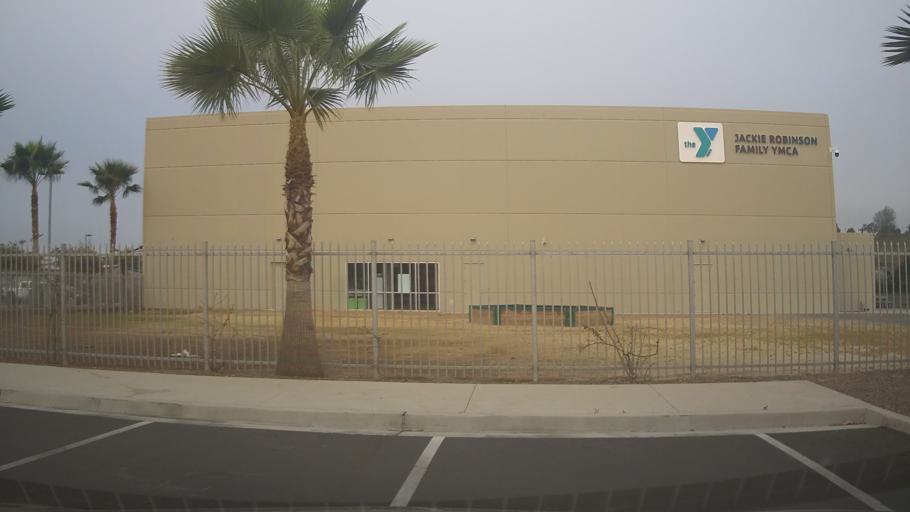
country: US
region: California
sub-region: San Diego County
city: National City
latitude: 32.7052
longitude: -117.0967
